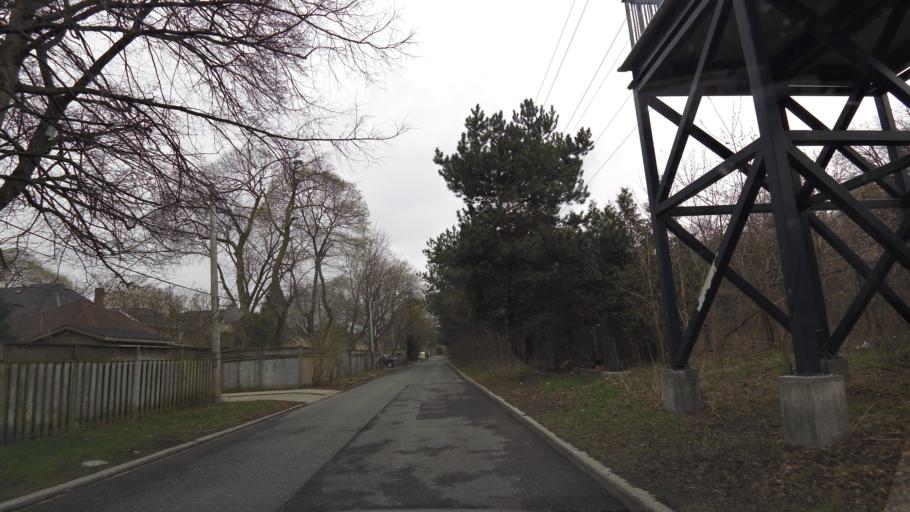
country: CA
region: Ontario
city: Toronto
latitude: 43.6855
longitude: -79.3786
